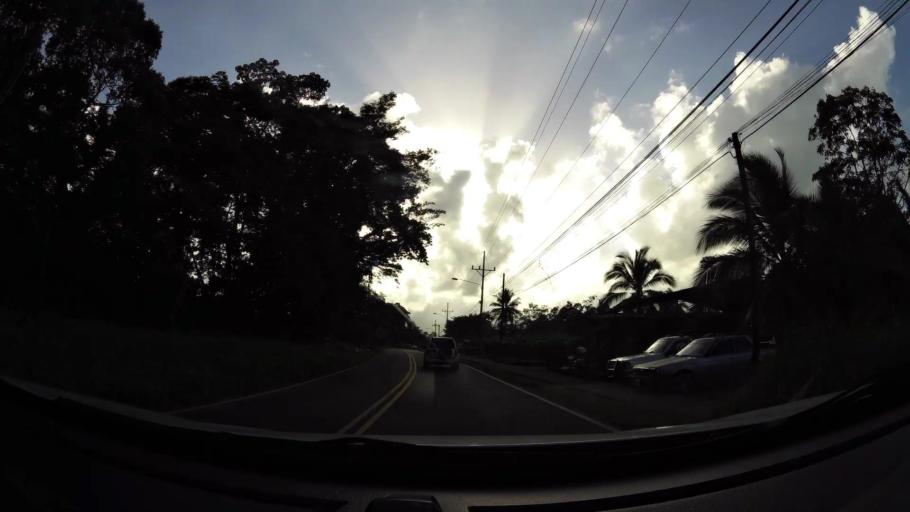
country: CR
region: Limon
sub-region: Canton de Siquirres
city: Siquirres
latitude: 10.0955
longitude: -83.5353
